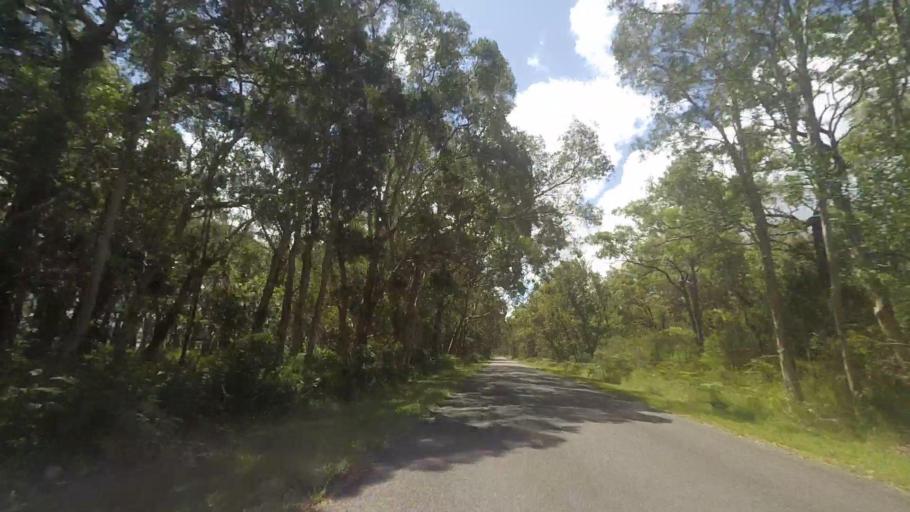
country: AU
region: New South Wales
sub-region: Great Lakes
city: Bulahdelah
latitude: -32.5134
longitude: 152.3214
